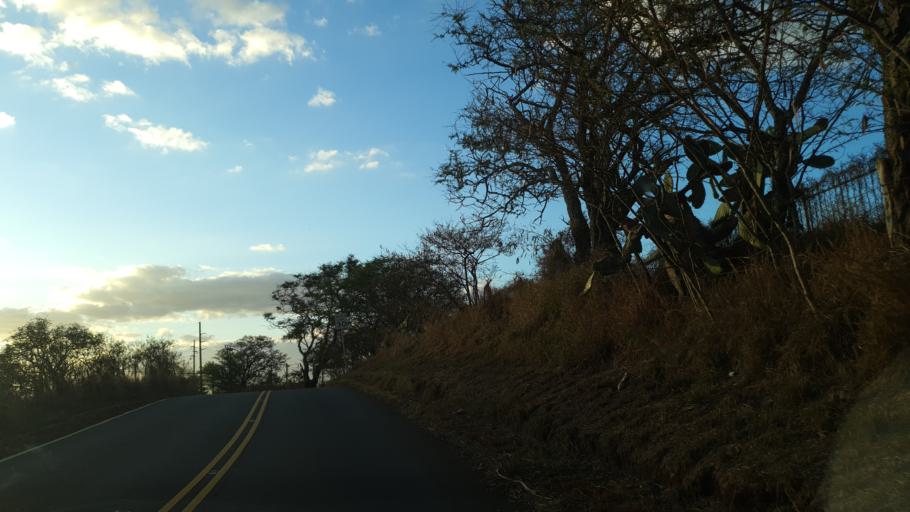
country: US
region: Hawaii
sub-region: Maui County
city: Pukalani
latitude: 20.7861
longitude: -156.3488
